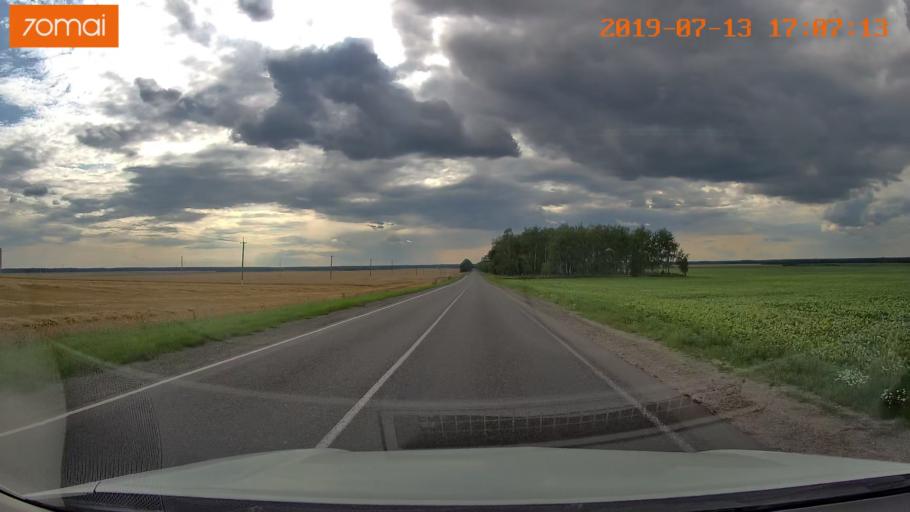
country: BY
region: Mogilev
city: Kirawsk
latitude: 53.2680
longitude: 29.3363
